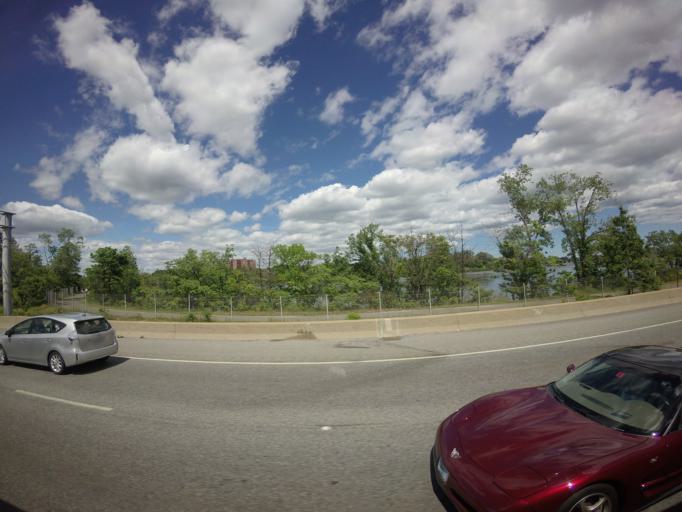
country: US
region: Massachusetts
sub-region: Middlesex County
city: Somerville
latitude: 42.4010
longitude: -71.0948
